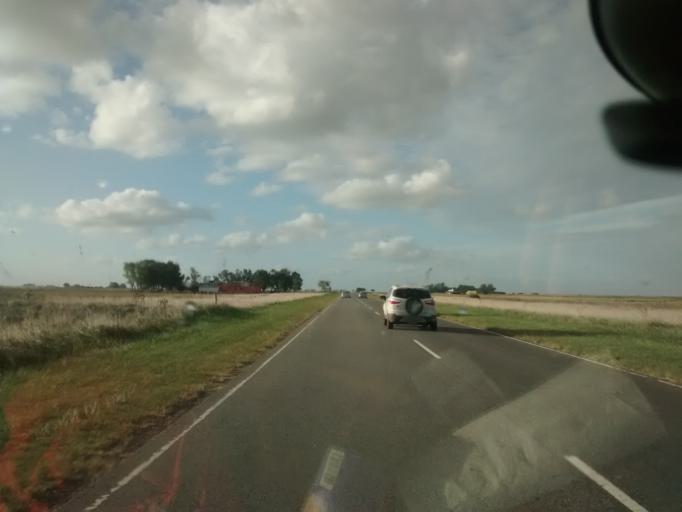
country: AR
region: Buenos Aires
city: Pila
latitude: -36.3367
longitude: -58.5804
